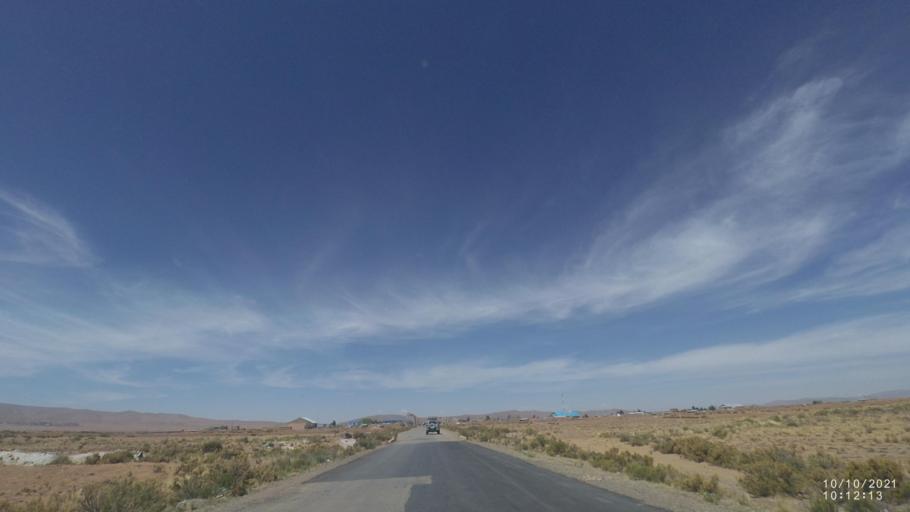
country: BO
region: La Paz
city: Eucaliptus
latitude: -17.4327
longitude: -67.5127
